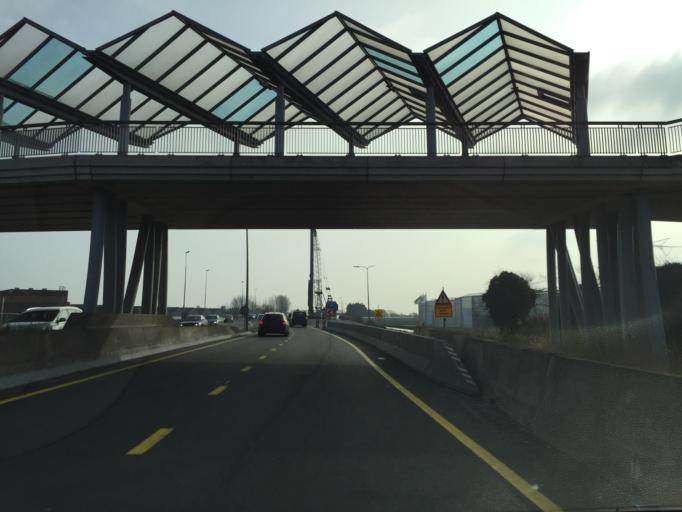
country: NL
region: South Holland
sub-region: Gemeente Westland
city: Naaldwijk
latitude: 51.9786
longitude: 4.2189
